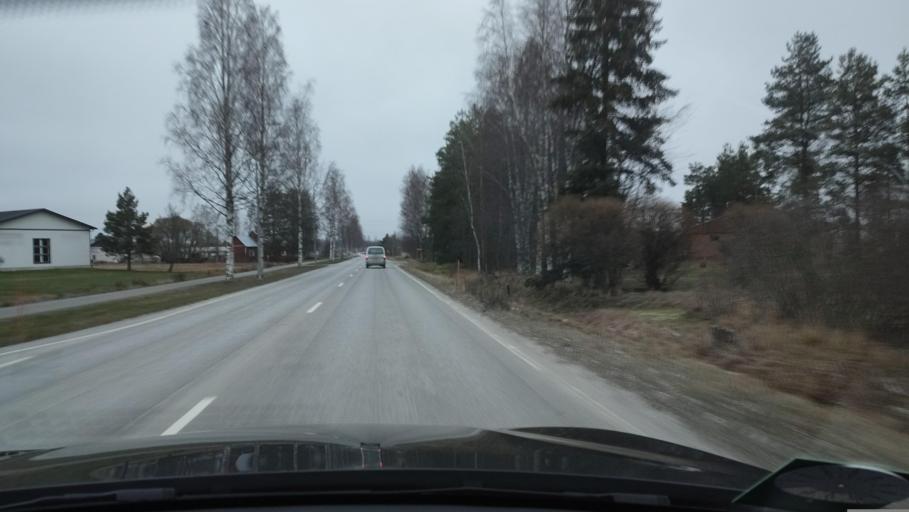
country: FI
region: Southern Ostrobothnia
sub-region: Suupohja
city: Kauhajoki
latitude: 62.4468
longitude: 22.2026
